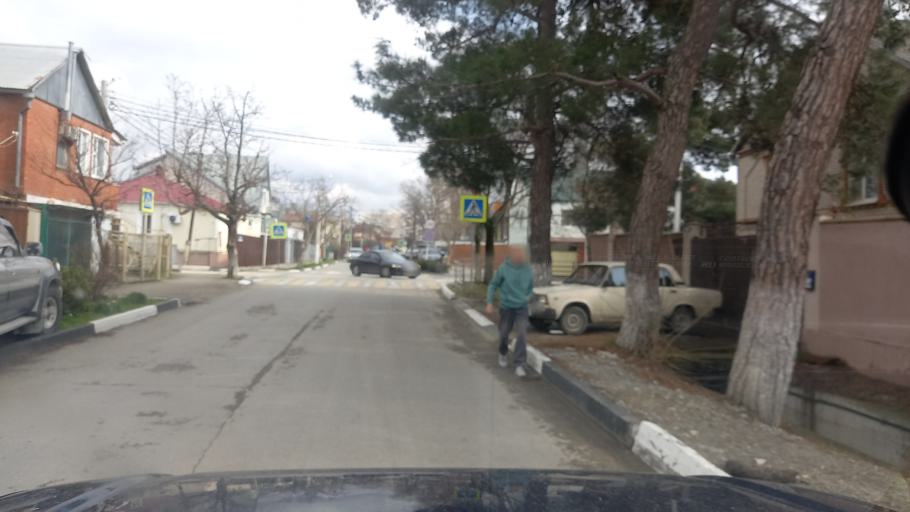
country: RU
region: Krasnodarskiy
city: Gelendzhik
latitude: 44.5586
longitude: 38.0895
